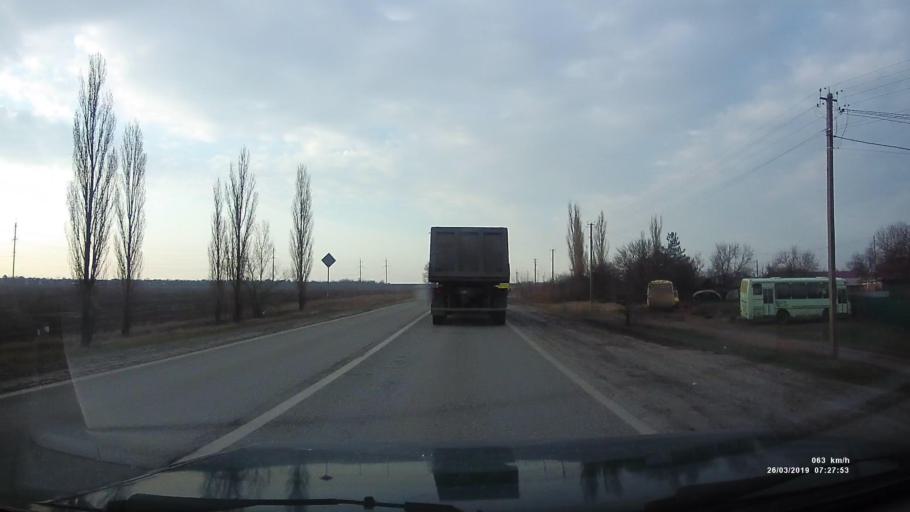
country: RU
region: Rostov
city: Taganrog
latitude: 47.2586
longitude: 38.8260
